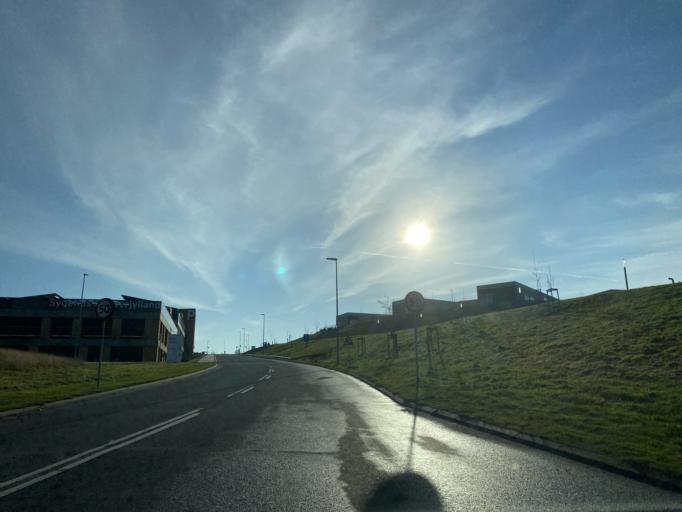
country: DK
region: South Denmark
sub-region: Aabenraa Kommune
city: Aabenraa
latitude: 55.0663
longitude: 9.3768
